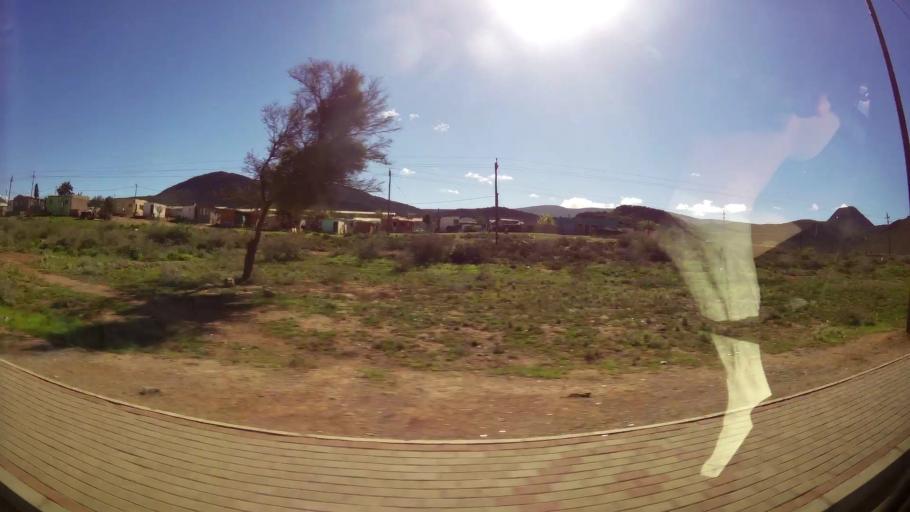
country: ZA
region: Western Cape
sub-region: Cape Winelands District Municipality
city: Ashton
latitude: -33.7690
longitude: 20.1486
